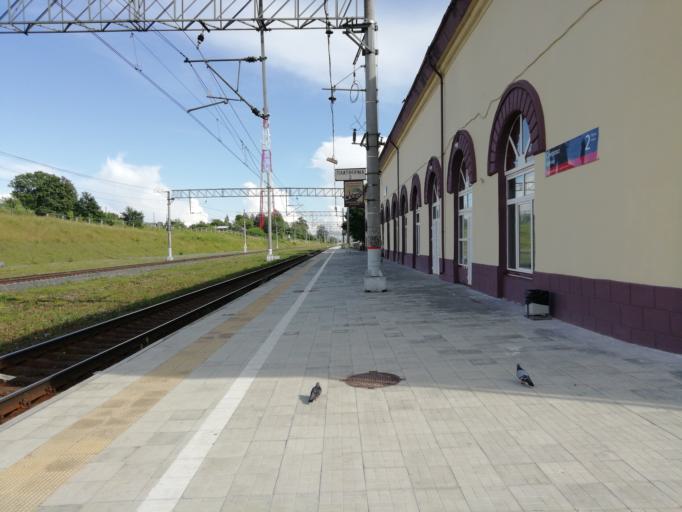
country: RU
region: Tverskaya
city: Spirovo
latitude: 57.4217
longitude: 34.9952
